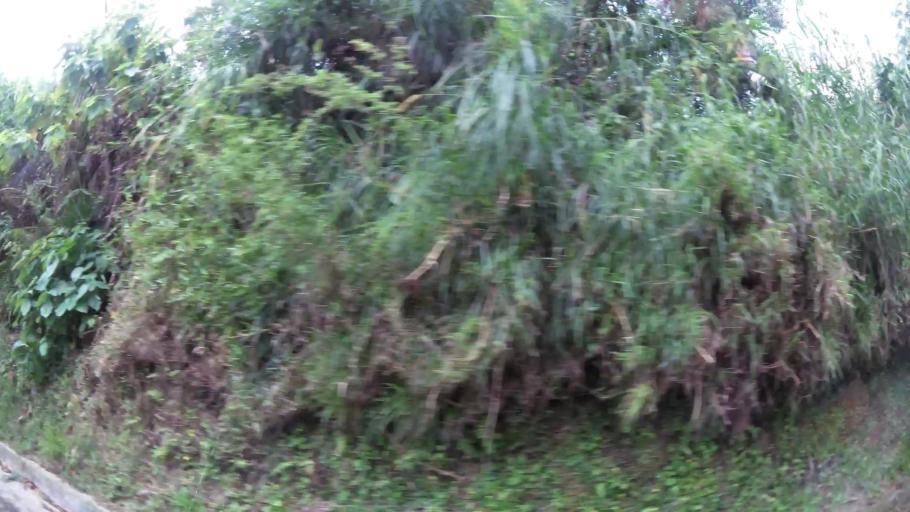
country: CO
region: Antioquia
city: La Estrella
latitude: 6.1735
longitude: -75.6610
